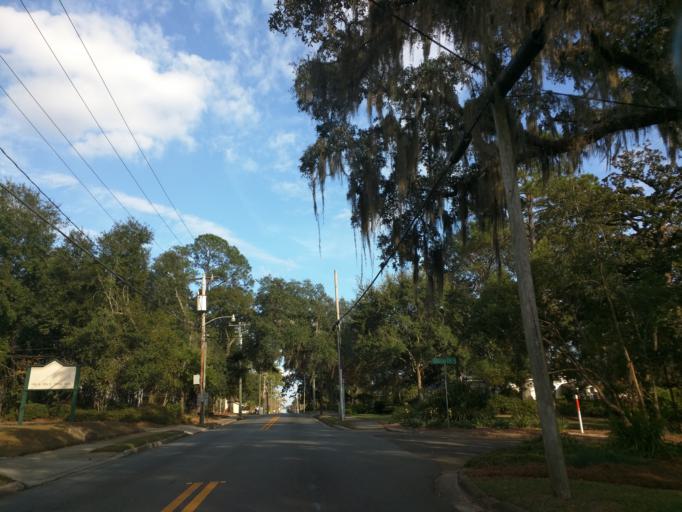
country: US
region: Florida
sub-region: Leon County
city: Tallahassee
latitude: 30.4417
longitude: -84.2667
